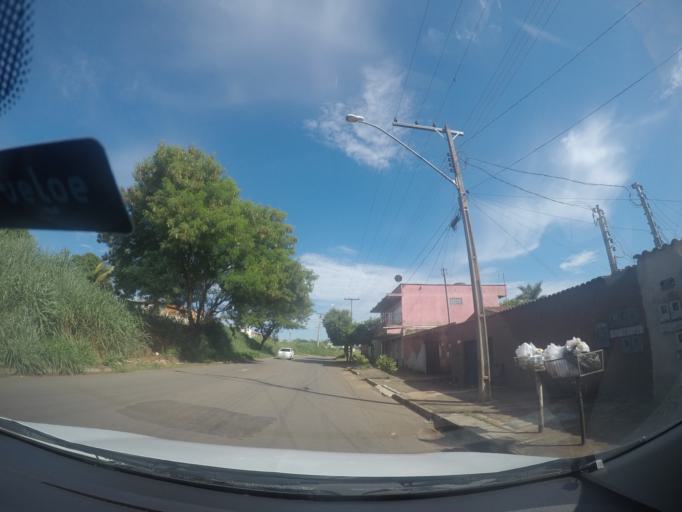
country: BR
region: Goias
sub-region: Goiania
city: Goiania
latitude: -16.6638
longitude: -49.2072
